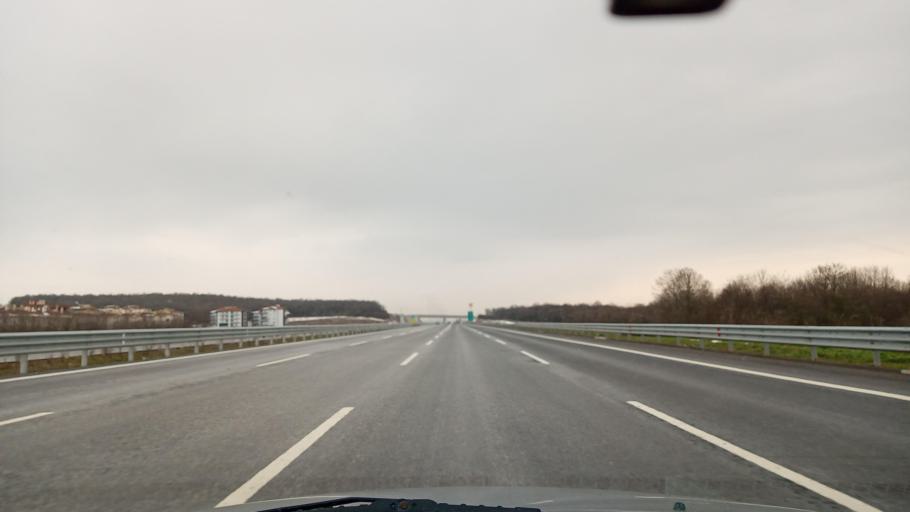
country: TR
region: Sakarya
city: Kazimpasa
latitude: 40.8450
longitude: 30.2680
